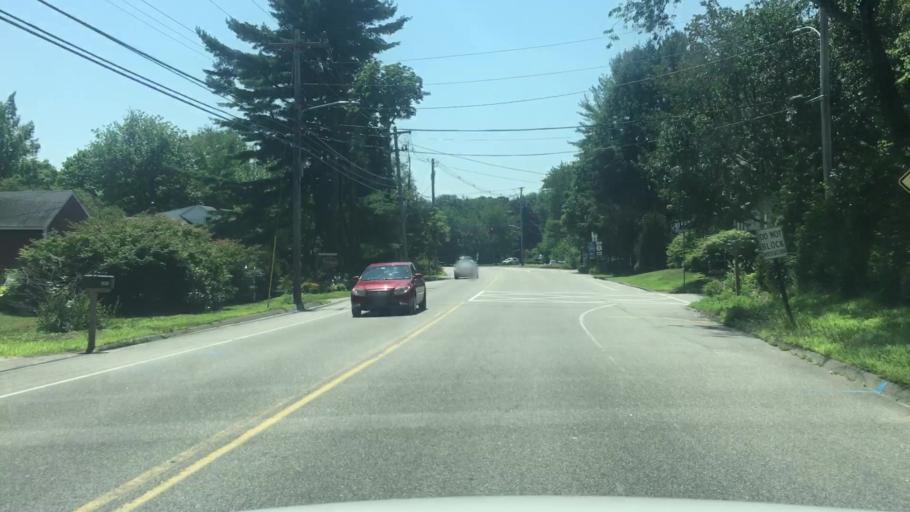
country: US
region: Maine
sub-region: Cumberland County
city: Falmouth
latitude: 43.7306
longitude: -70.2409
